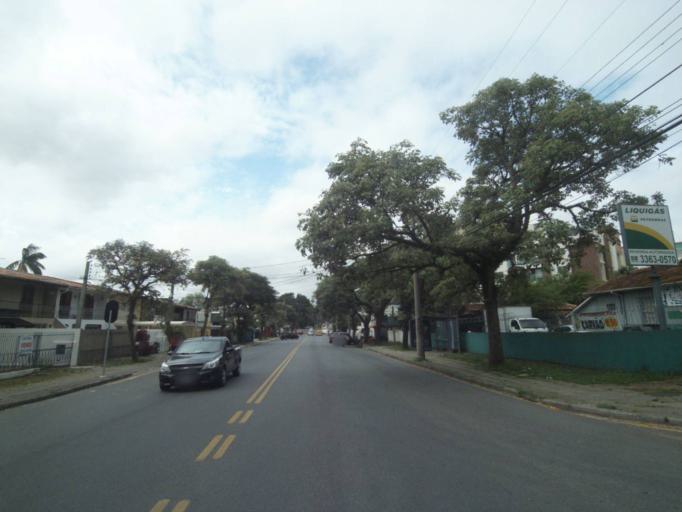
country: BR
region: Parana
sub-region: Curitiba
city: Curitiba
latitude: -25.4161
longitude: -49.2478
